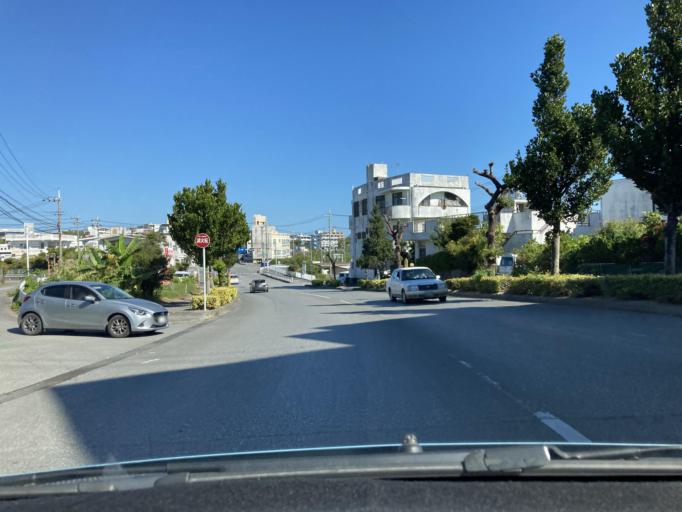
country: JP
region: Okinawa
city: Gushikawa
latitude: 26.3489
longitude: 127.8367
